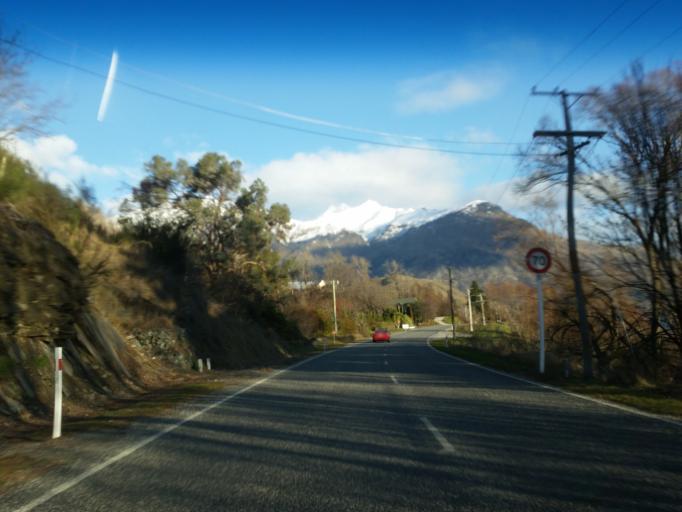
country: NZ
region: Otago
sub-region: Queenstown-Lakes District
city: Arrowtown
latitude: -44.9697
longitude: 168.8177
